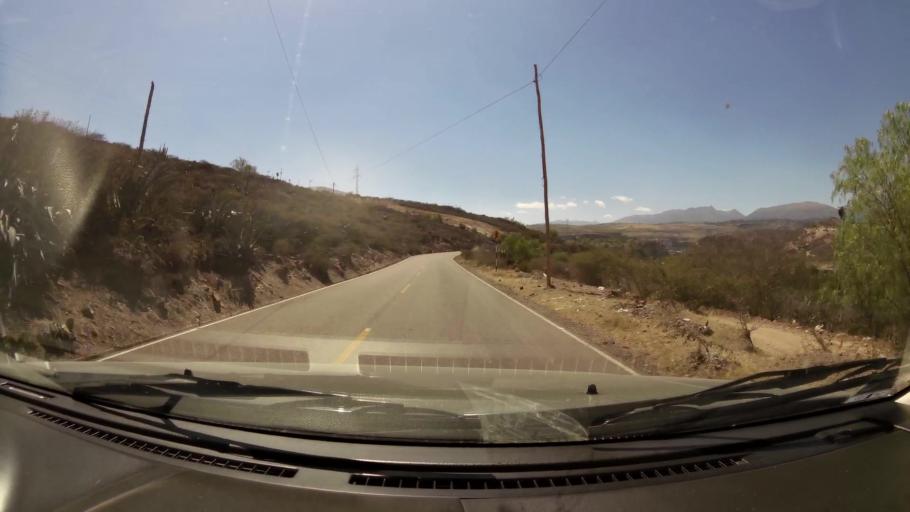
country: PE
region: Ayacucho
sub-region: Provincia de Huamanga
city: Pacaycasa
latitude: -13.0717
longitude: -74.2219
